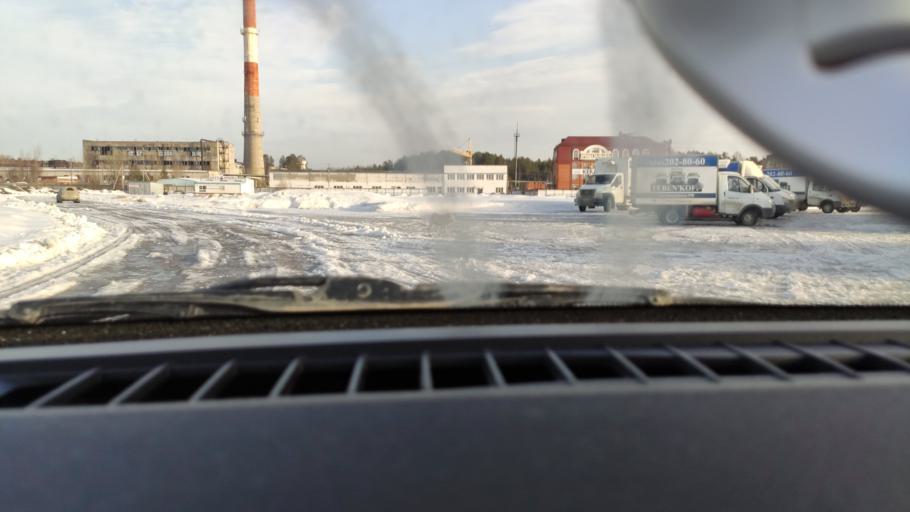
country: RU
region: Perm
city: Perm
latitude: 58.0371
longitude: 56.2032
